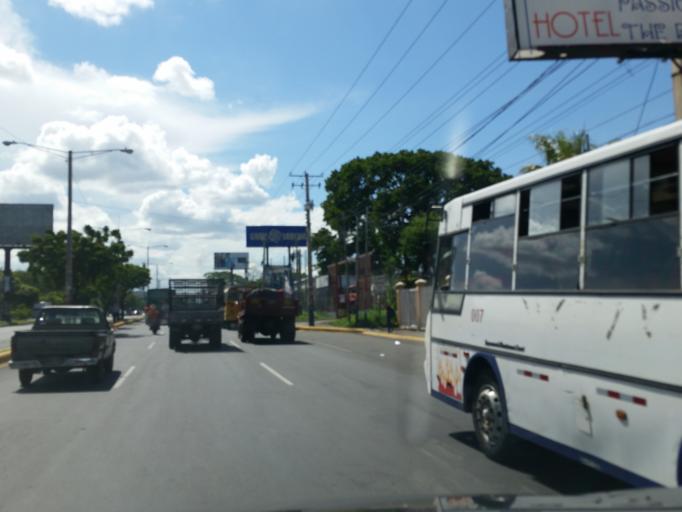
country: NI
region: Managua
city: Managua
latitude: 12.1495
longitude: -86.2117
